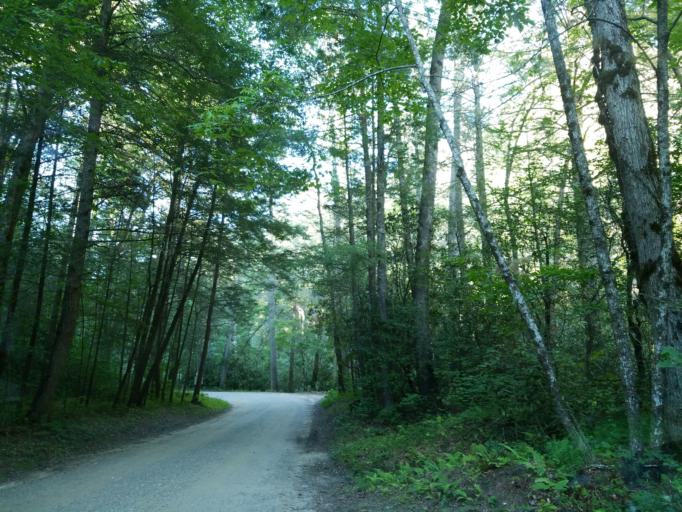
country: US
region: Georgia
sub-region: Union County
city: Blairsville
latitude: 34.7616
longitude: -84.0723
